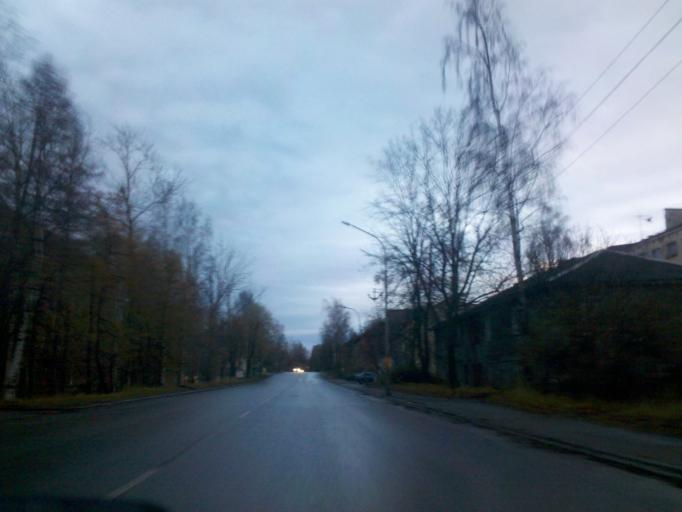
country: RU
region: Republic of Karelia
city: Petrozavodsk
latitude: 61.7839
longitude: 34.3978
